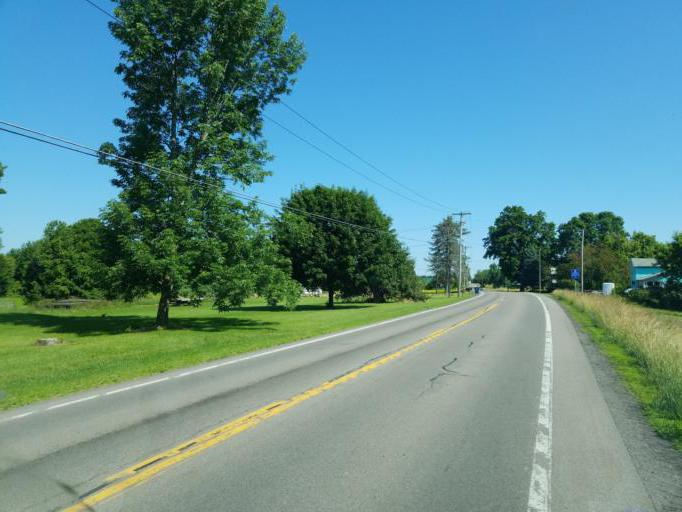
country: US
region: New York
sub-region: Wayne County
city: Clyde
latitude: 43.0981
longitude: -76.8678
